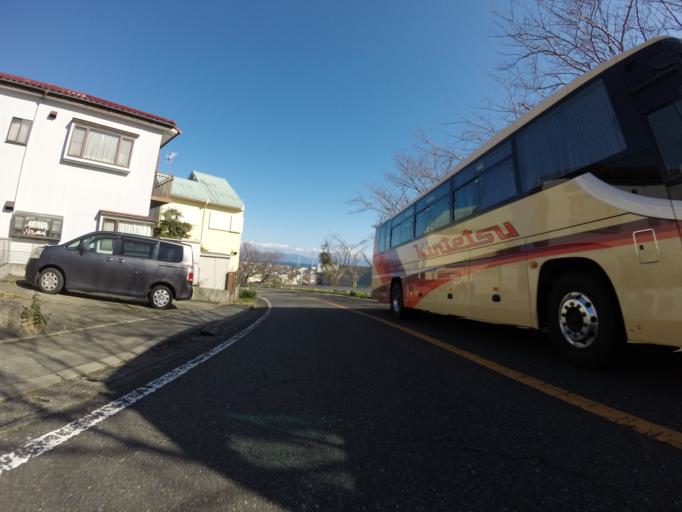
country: JP
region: Shizuoka
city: Shizuoka-shi
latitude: 34.9792
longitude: 138.4915
